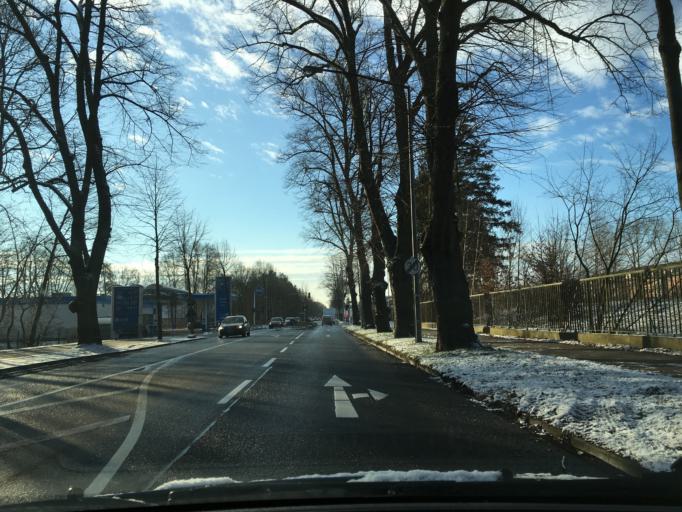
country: DE
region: Lower Saxony
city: Lueneburg
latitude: 53.2278
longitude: 10.4057
